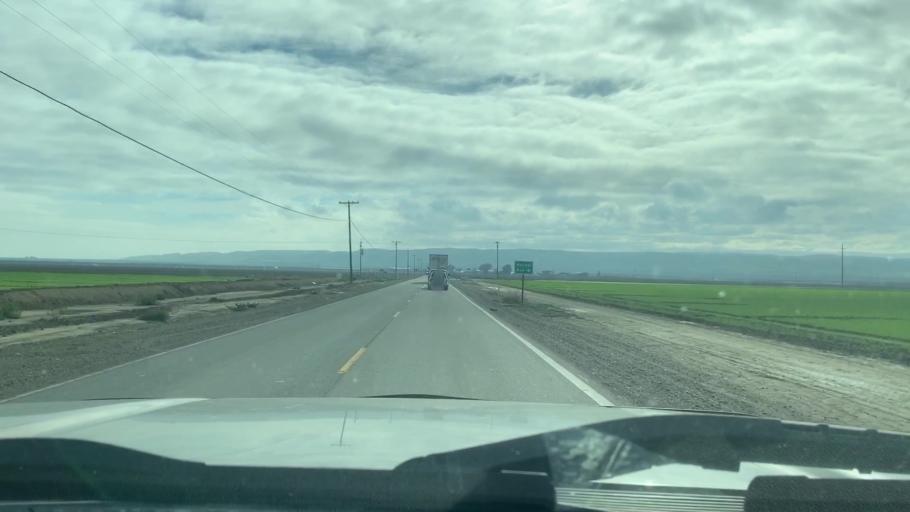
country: US
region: California
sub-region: Merced County
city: Los Banos
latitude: 36.9711
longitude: -120.8375
